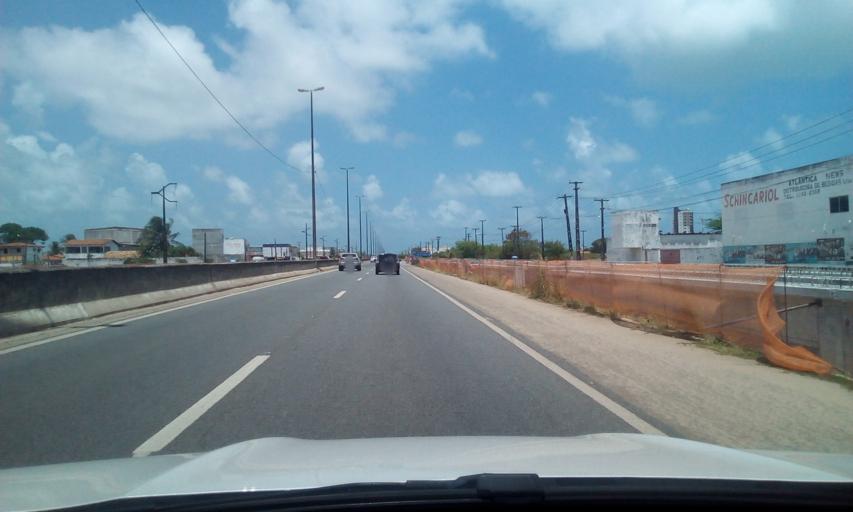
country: BR
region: Paraiba
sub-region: Cabedelo
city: Cabedelo
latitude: -7.0347
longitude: -34.8423
